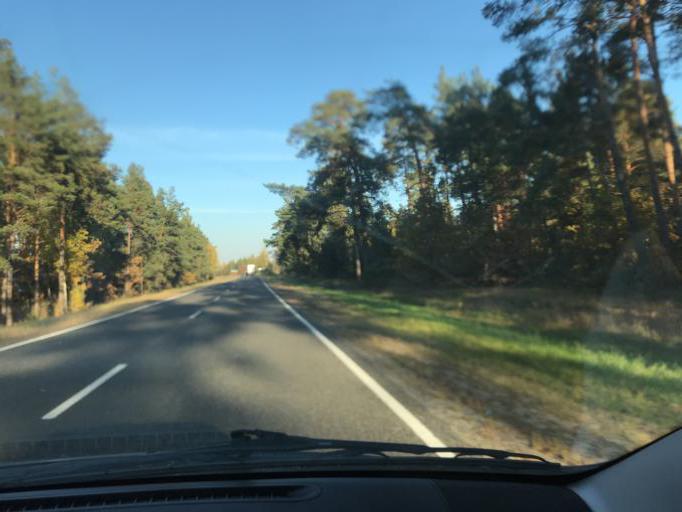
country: BY
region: Brest
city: Stolin
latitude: 51.8283
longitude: 26.7096
